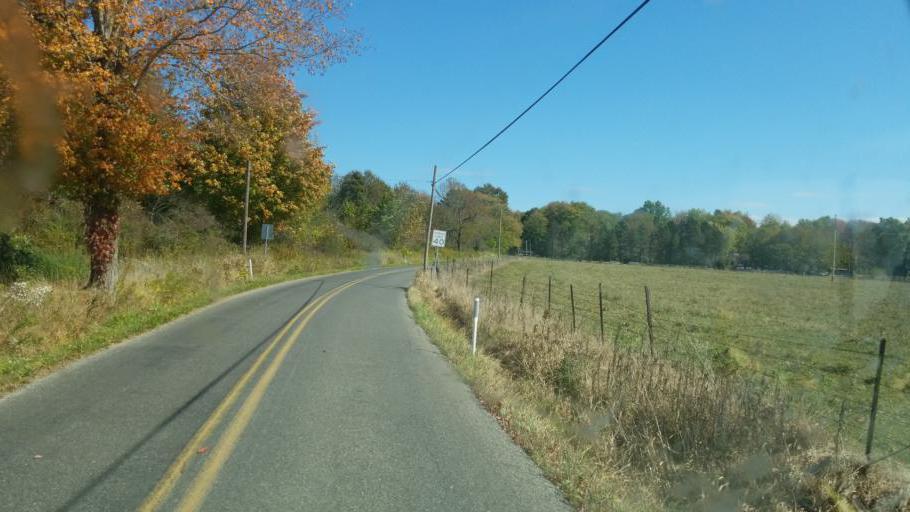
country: US
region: Pennsylvania
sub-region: Mercer County
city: Reynolds Heights
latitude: 41.3674
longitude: -80.3646
